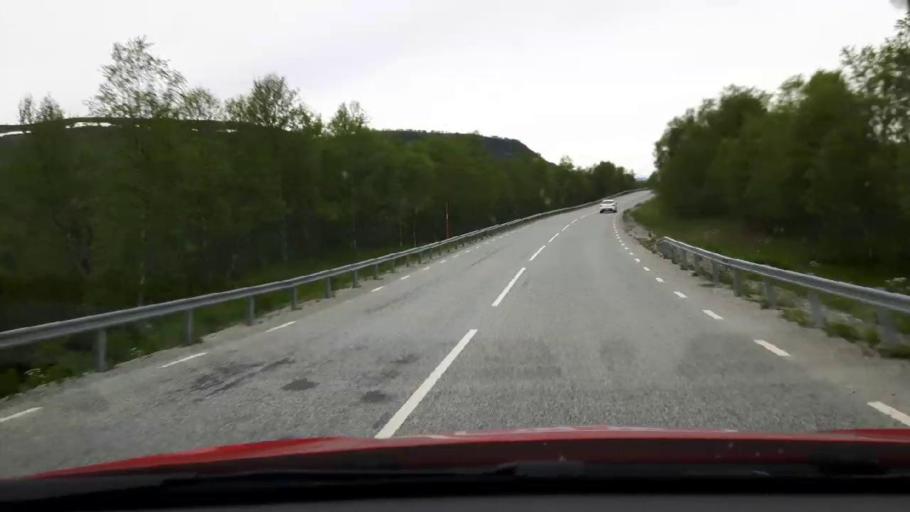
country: NO
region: Sor-Trondelag
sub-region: Tydal
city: Aas
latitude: 62.6771
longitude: 12.4217
